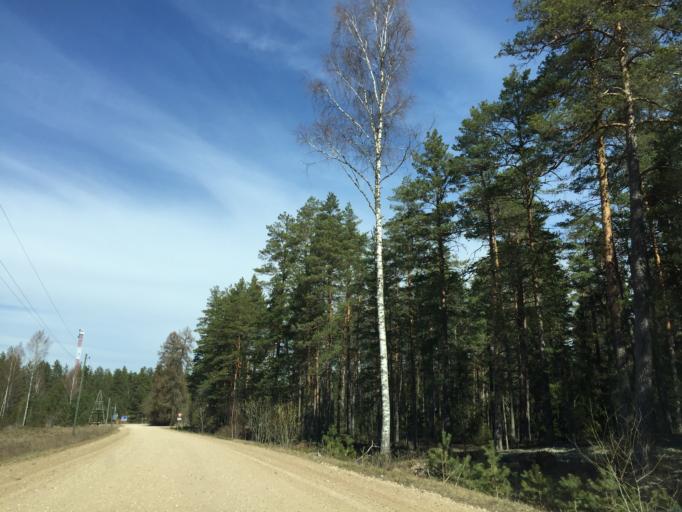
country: LV
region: Strenci
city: Seda
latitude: 57.6489
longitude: 25.8641
